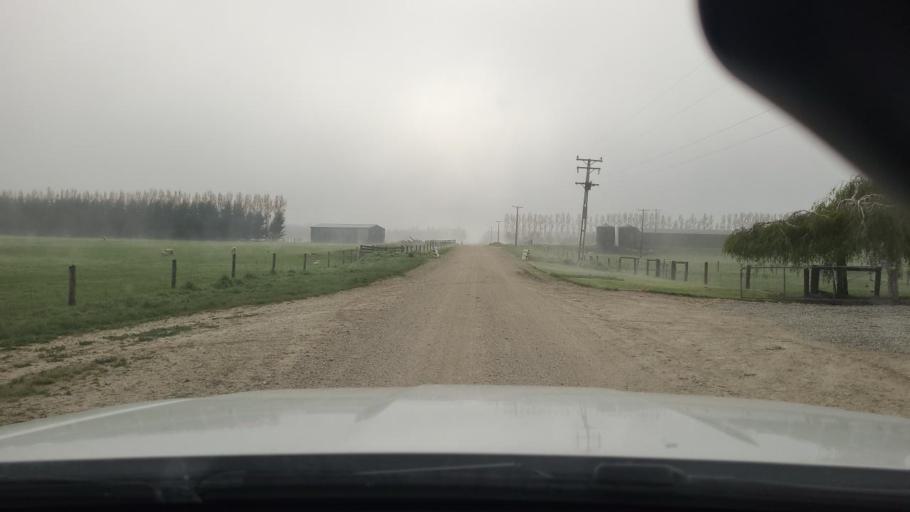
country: NZ
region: Otago
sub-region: Queenstown-Lakes District
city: Kingston
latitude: -45.6040
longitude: 168.9641
